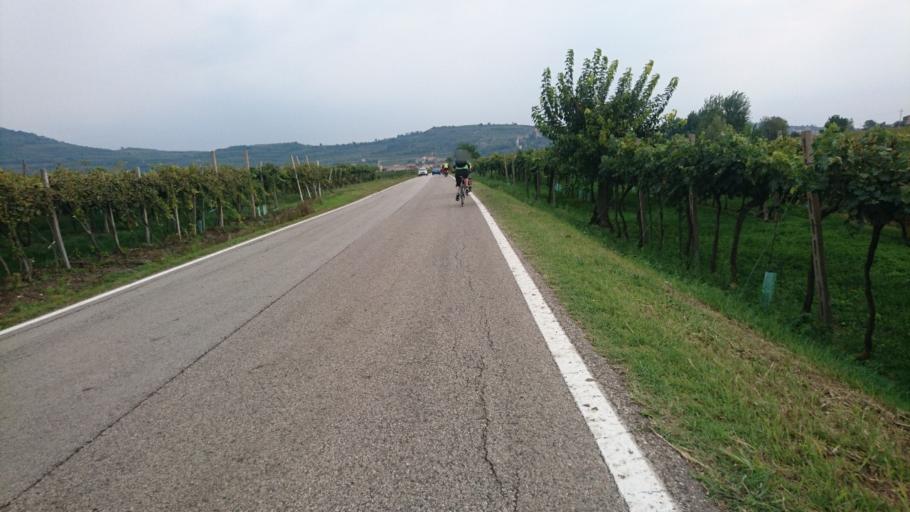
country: IT
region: Veneto
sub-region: Provincia di Verona
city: Soave
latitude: 45.4272
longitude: 11.2297
